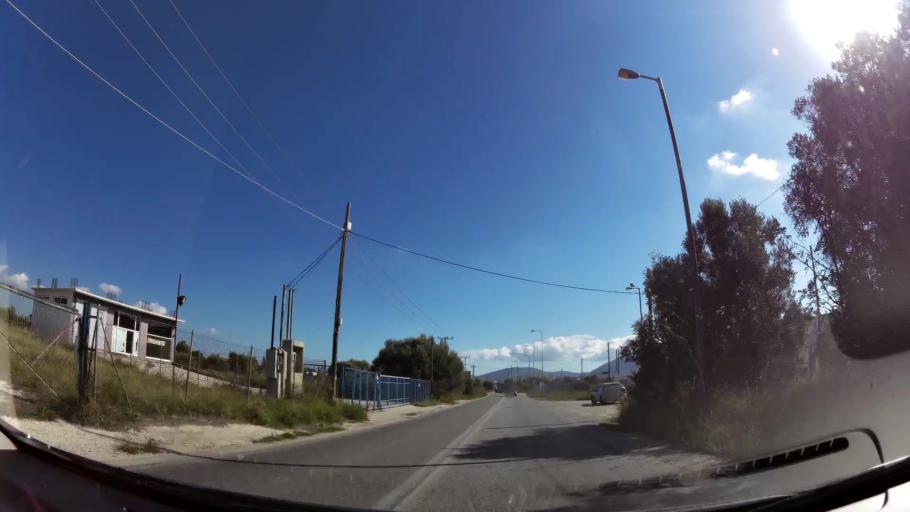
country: GR
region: Attica
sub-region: Nomarchia Anatolikis Attikis
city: Markopoulo
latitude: 37.8874
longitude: 23.9029
